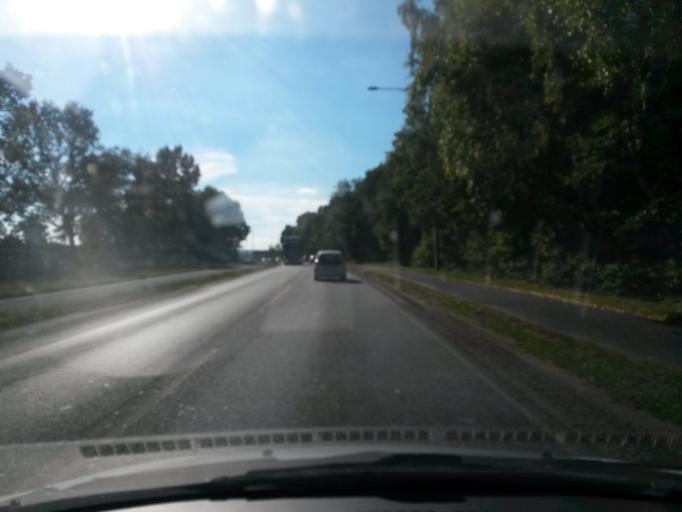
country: DK
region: Central Jutland
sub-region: Silkeborg Kommune
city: Silkeborg
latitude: 56.1796
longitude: 9.5325
